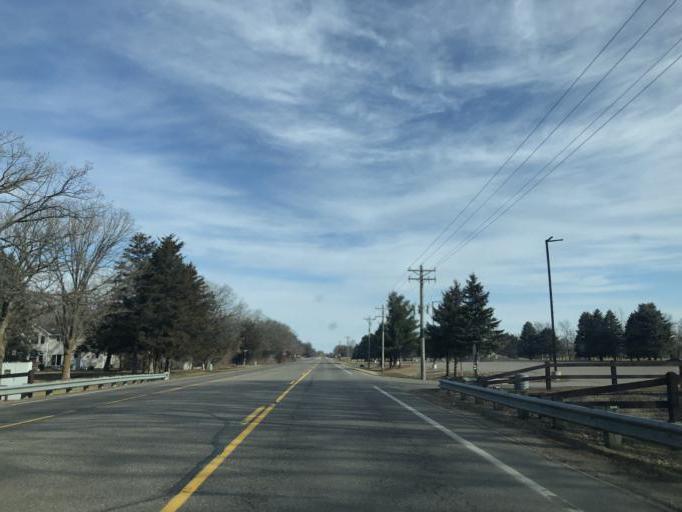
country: US
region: Minnesota
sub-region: Sherburne County
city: Becker
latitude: 45.4052
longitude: -93.8705
